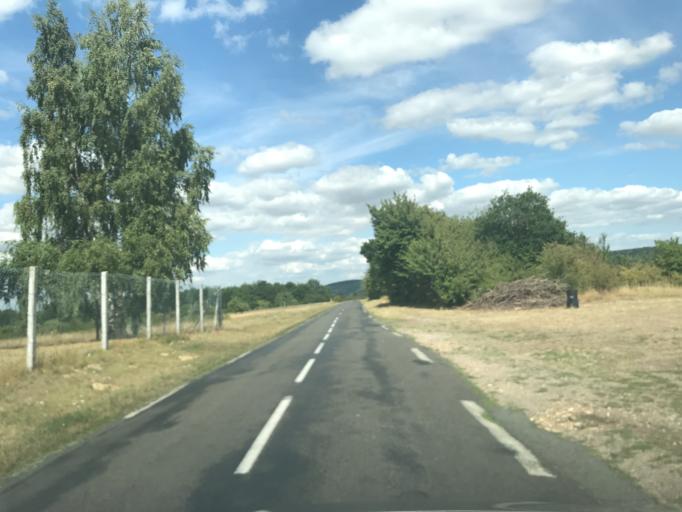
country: FR
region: Haute-Normandie
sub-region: Departement de l'Eure
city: Courcelles-sur-Seine
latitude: 49.2101
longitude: 1.3546
